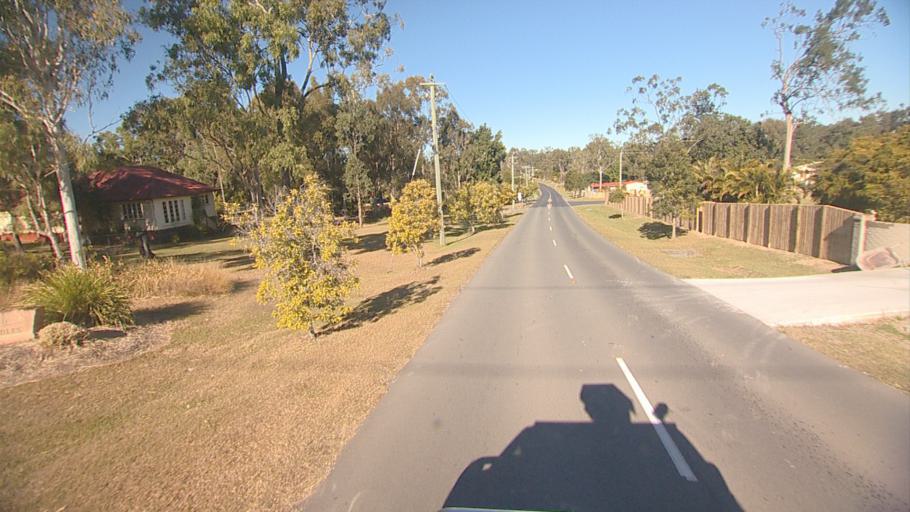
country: AU
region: Queensland
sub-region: Logan
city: North Maclean
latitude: -27.7390
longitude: 152.9696
